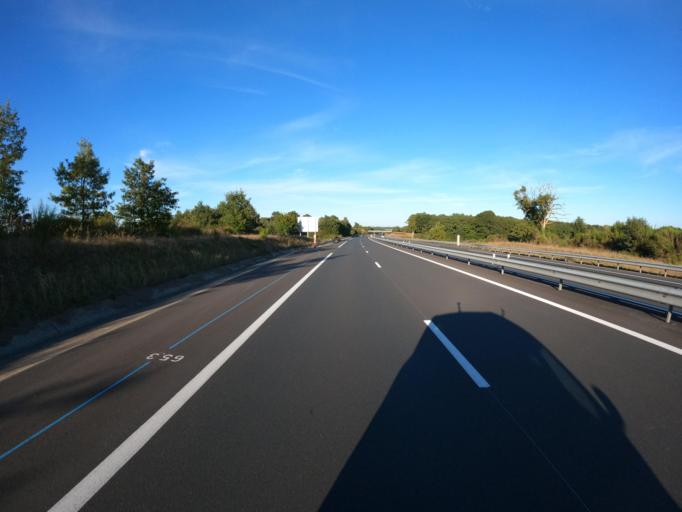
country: FR
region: Pays de la Loire
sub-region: Departement de la Vendee
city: Mortagne-sur-Sevre
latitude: 46.9556
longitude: -0.9388
